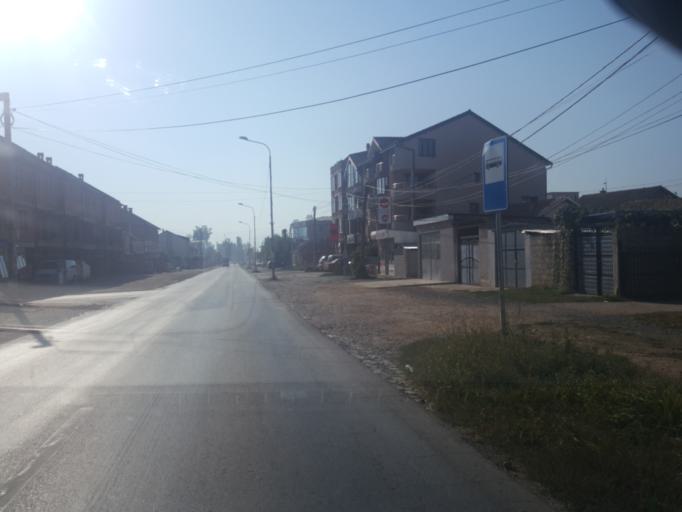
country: XK
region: Gjakova
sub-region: Komuna e Gjakoves
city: Gjakove
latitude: 42.4016
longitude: 20.4143
